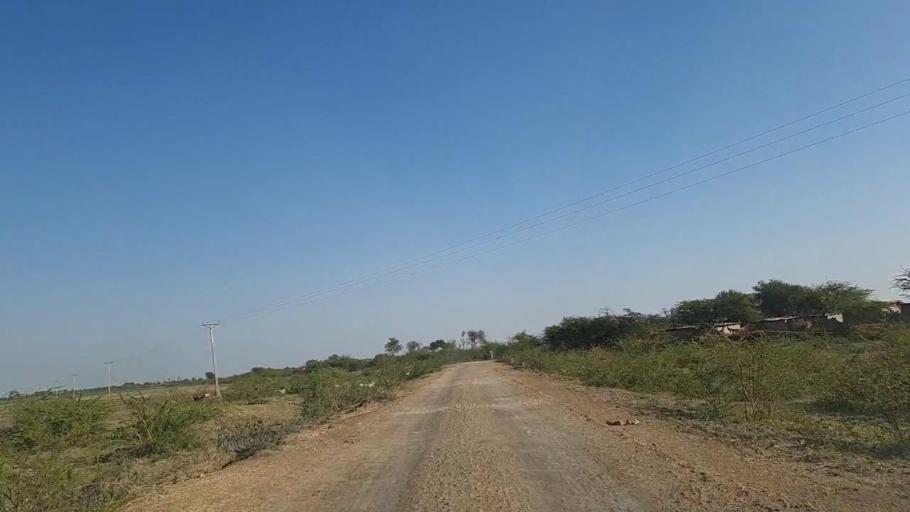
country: PK
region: Sindh
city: Naukot
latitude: 24.9472
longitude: 69.3346
